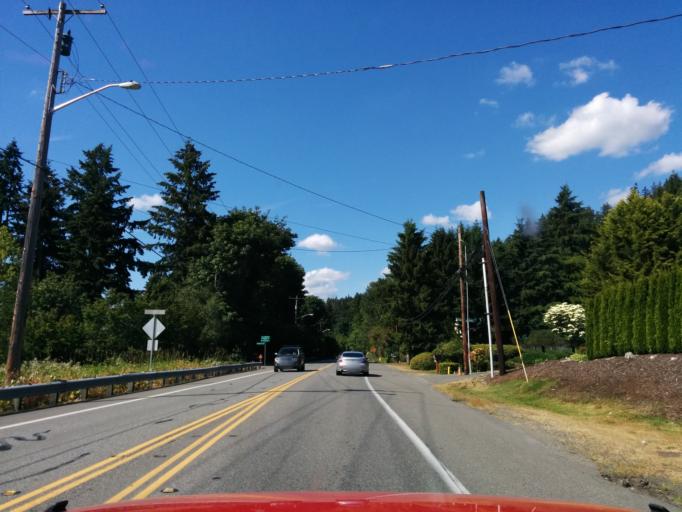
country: US
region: Washington
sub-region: King County
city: Sammamish
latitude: 47.6142
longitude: -122.0680
